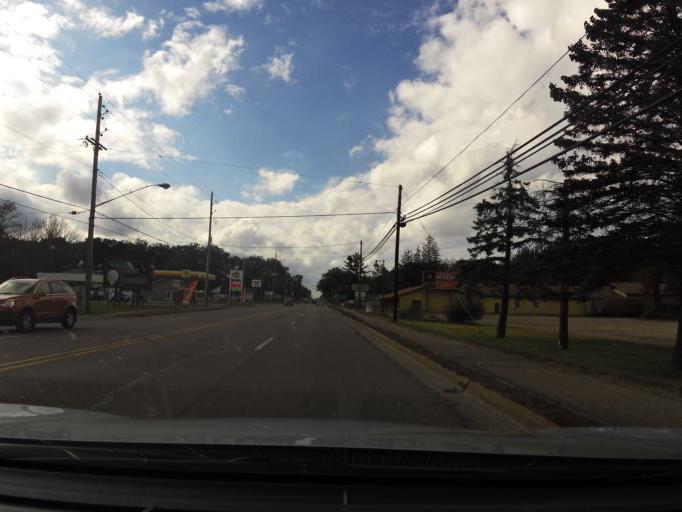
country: US
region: Michigan
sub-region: Roscommon County
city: Prudenville
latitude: 44.2986
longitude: -84.6631
